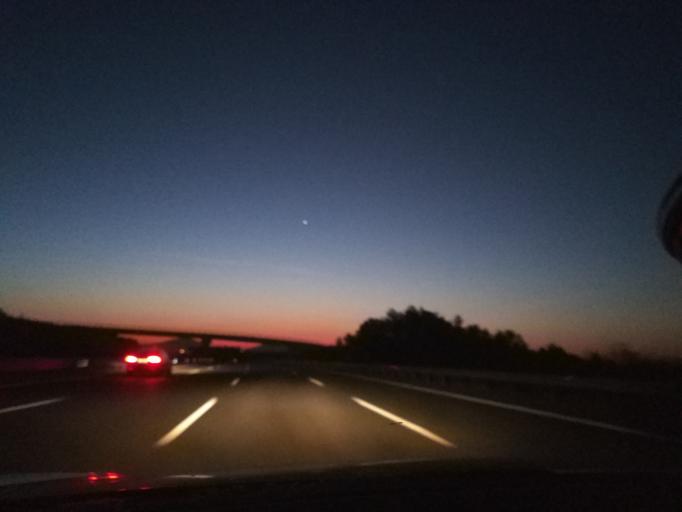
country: TR
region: Istanbul
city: Sancaktepe
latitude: 41.0428
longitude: 29.2134
